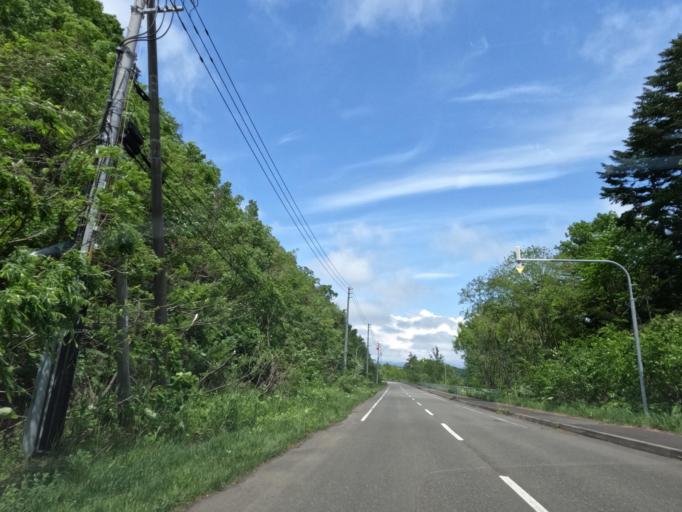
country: JP
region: Hokkaido
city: Tobetsu
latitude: 43.3214
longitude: 141.5684
